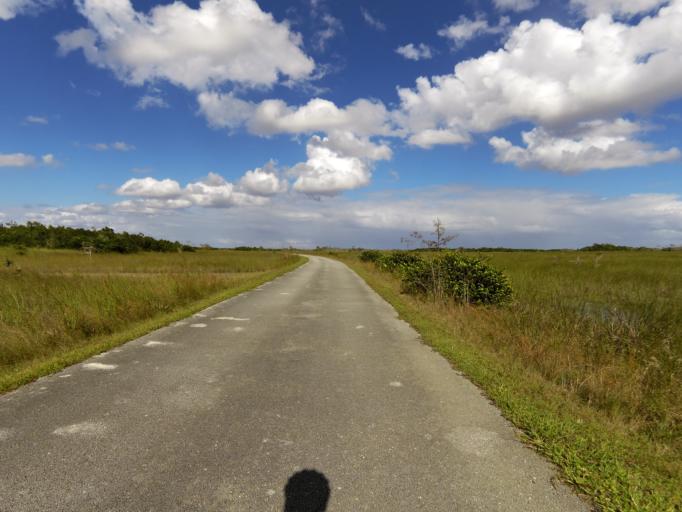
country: US
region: Florida
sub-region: Miami-Dade County
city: The Hammocks
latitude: 25.7137
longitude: -80.7600
